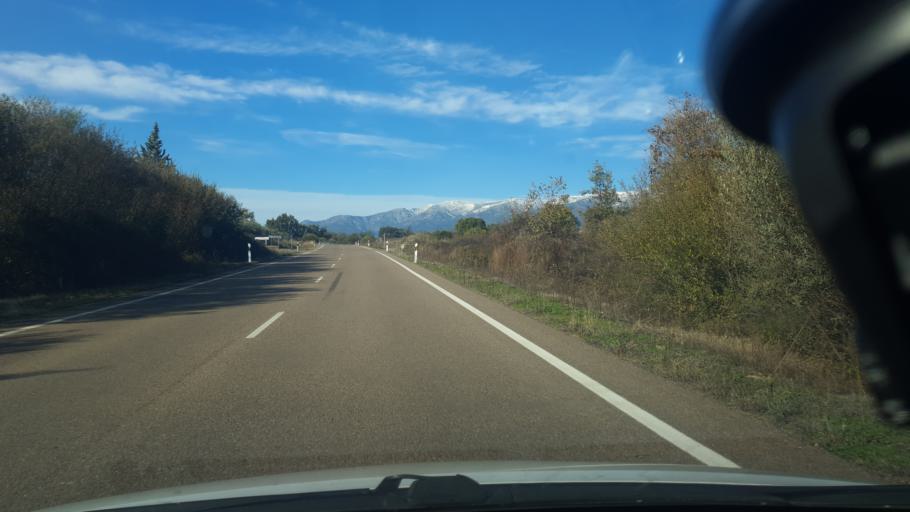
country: ES
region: Castille and Leon
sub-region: Provincia de Avila
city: Candeleda
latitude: 40.1371
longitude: -5.2410
